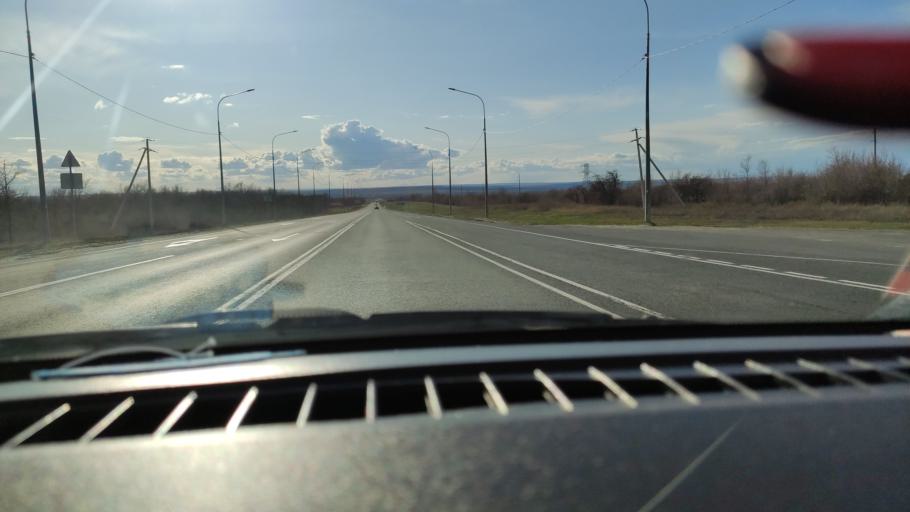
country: RU
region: Saratov
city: Yelshanka
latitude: 51.8262
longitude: 46.2835
